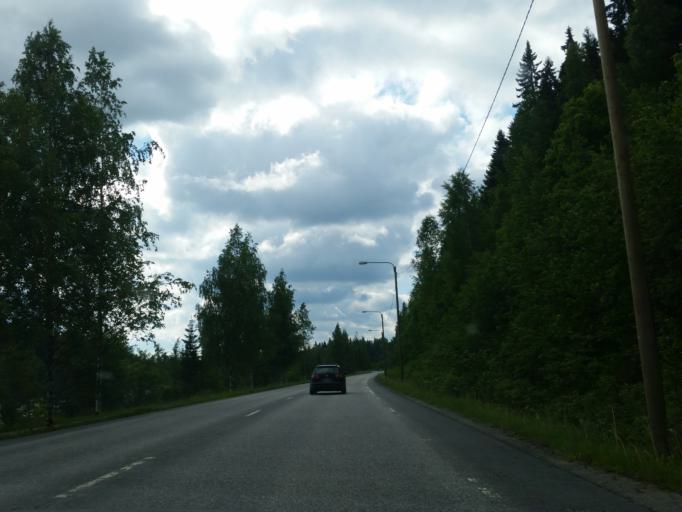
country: FI
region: Northern Savo
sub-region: Kuopio
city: Kuopio
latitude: 62.8447
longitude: 27.5519
